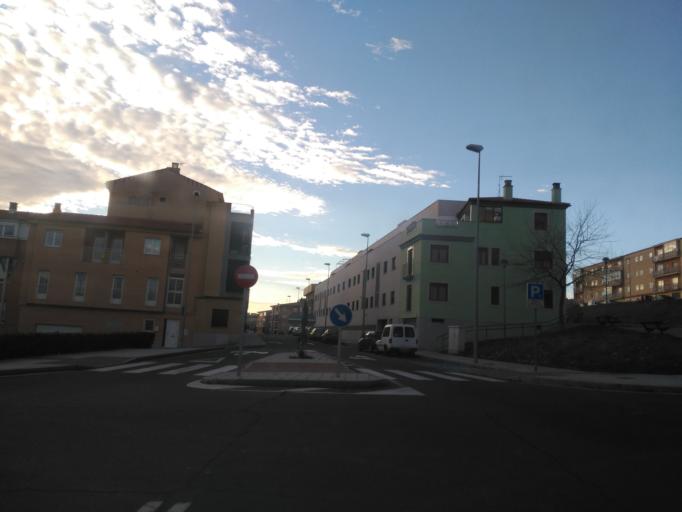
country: ES
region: Castille and Leon
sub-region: Provincia de Salamanca
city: Salamanca
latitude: 40.9794
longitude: -5.6726
